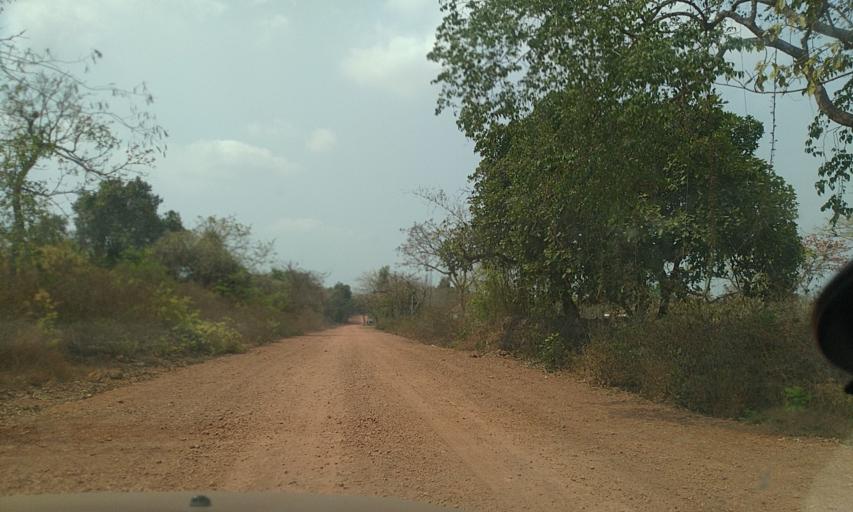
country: IN
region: Goa
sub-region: North Goa
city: Goa Velha
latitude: 15.4775
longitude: 73.9099
